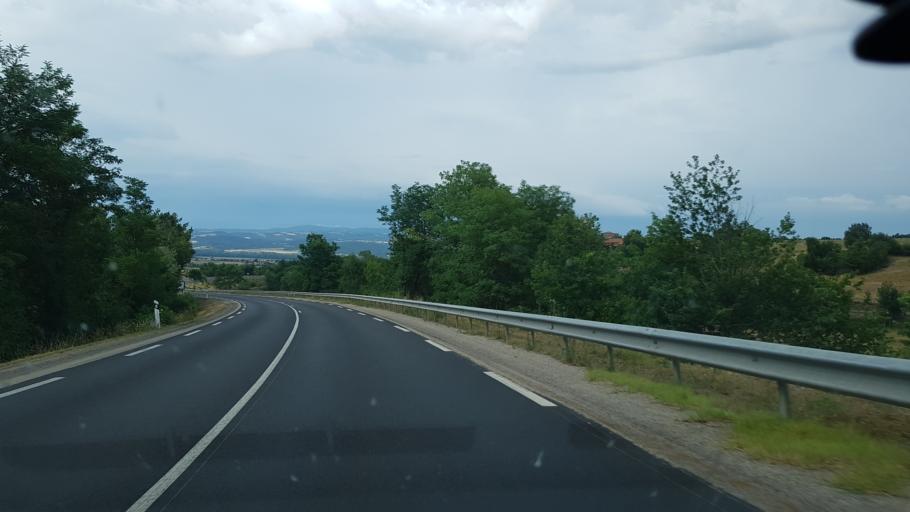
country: FR
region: Auvergne
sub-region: Departement de la Haute-Loire
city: Brioude
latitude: 45.2808
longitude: 3.3534
